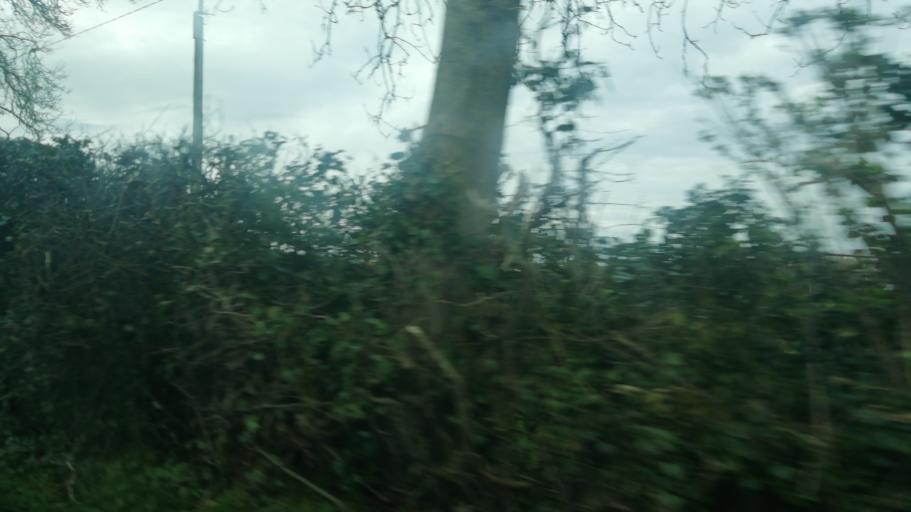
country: IE
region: Leinster
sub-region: Kildare
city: Maynooth
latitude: 53.3549
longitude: -6.6376
